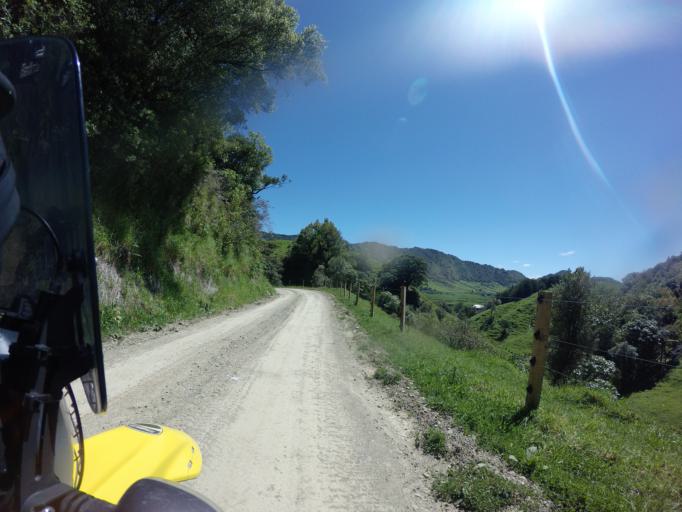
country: NZ
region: Bay of Plenty
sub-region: Opotiki District
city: Opotiki
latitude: -38.4041
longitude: 177.4542
